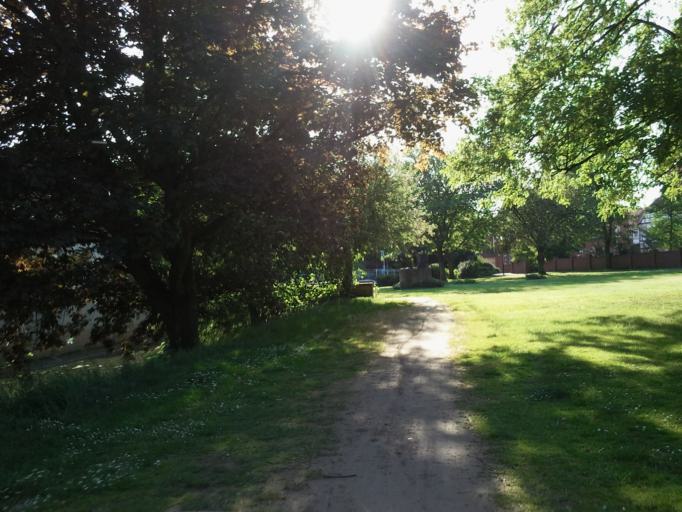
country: DE
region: Lower Saxony
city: Nienburg
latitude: 52.6371
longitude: 9.2099
